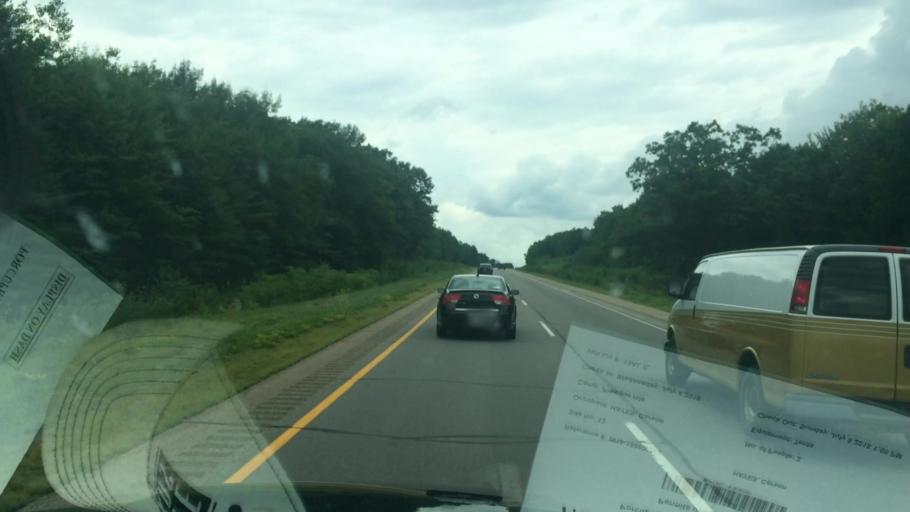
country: US
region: Wisconsin
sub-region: Marathon County
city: Mosinee
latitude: 44.6995
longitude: -89.6486
